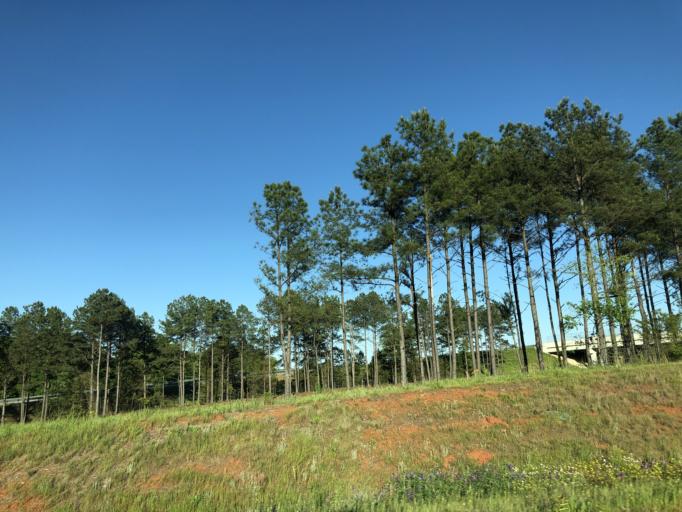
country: US
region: Georgia
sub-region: Oconee County
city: Watkinsville
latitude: 33.9175
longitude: -83.4611
